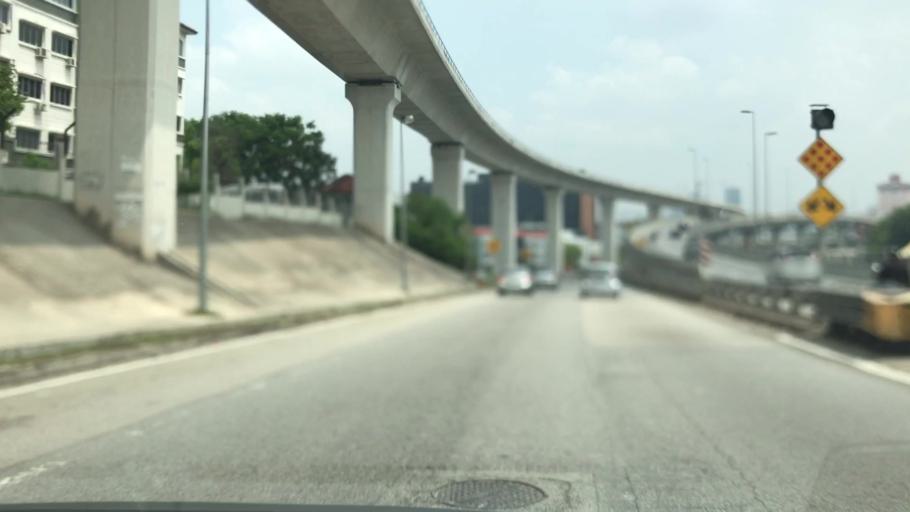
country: MY
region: Selangor
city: Subang Jaya
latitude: 3.0499
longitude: 101.6271
